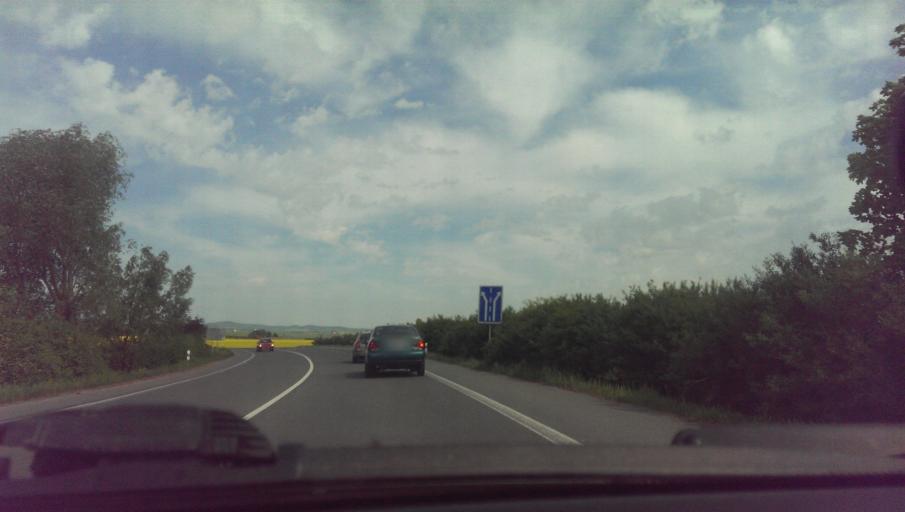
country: CZ
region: Zlin
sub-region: Okres Uherske Hradiste
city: Stare Mesto
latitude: 49.0884
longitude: 17.4492
